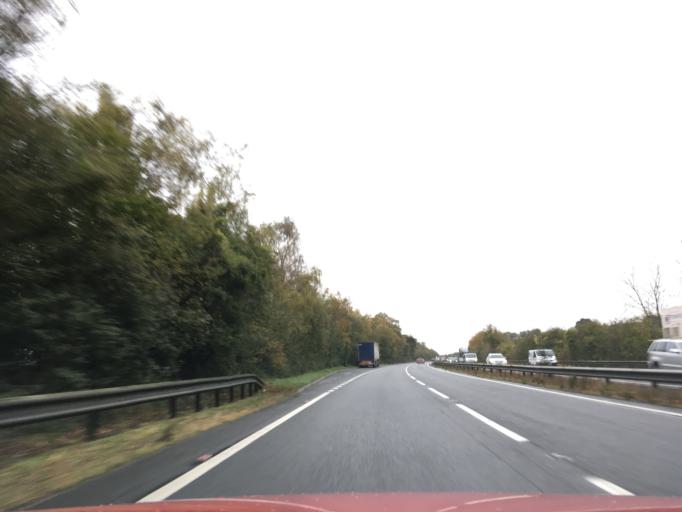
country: GB
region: England
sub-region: Hampshire
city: Overton
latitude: 51.2601
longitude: -1.3385
